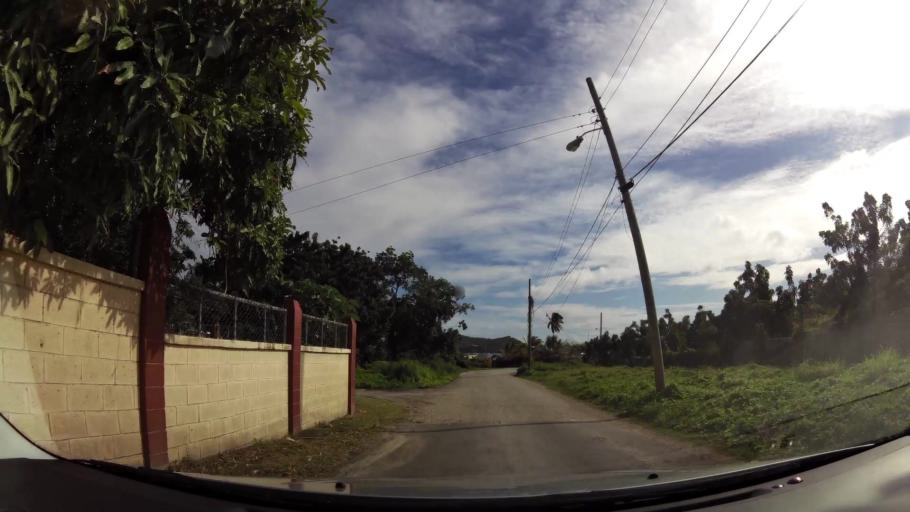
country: AG
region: Saint Paul
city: Falmouth
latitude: 17.0242
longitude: -61.7797
